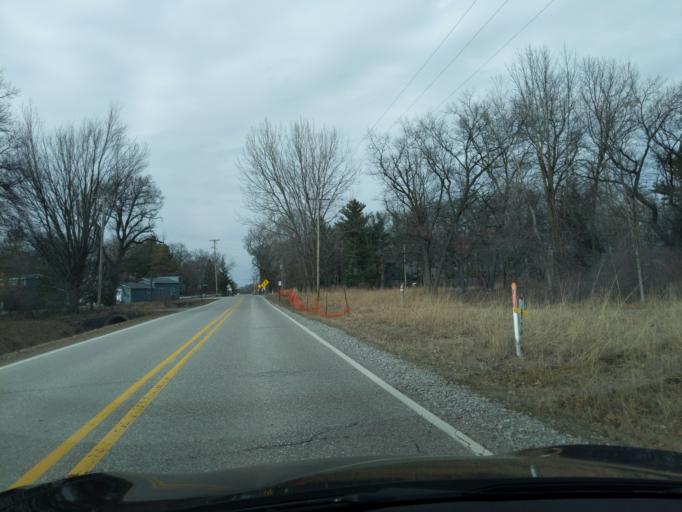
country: US
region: Michigan
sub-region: Bay County
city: Bay City
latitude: 43.6687
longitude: -83.9122
